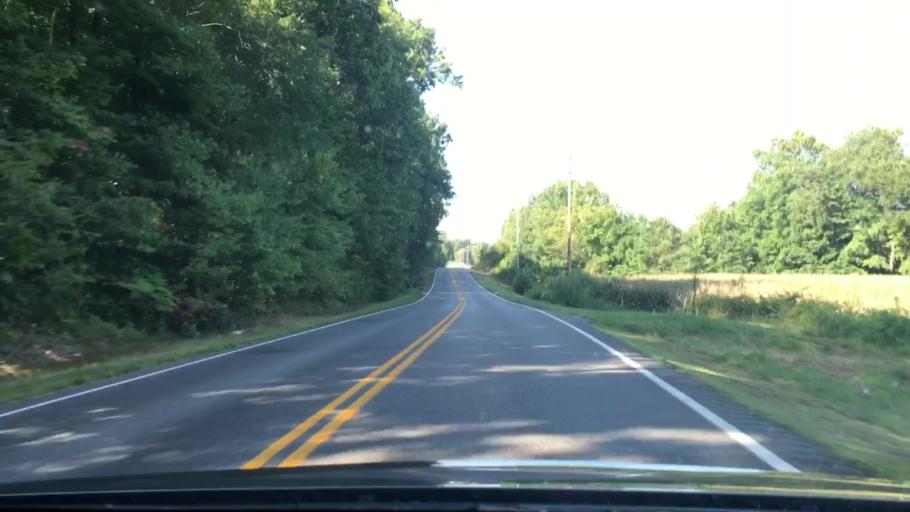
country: US
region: Kentucky
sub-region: Marshall County
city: Benton
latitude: 36.7783
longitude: -88.4762
